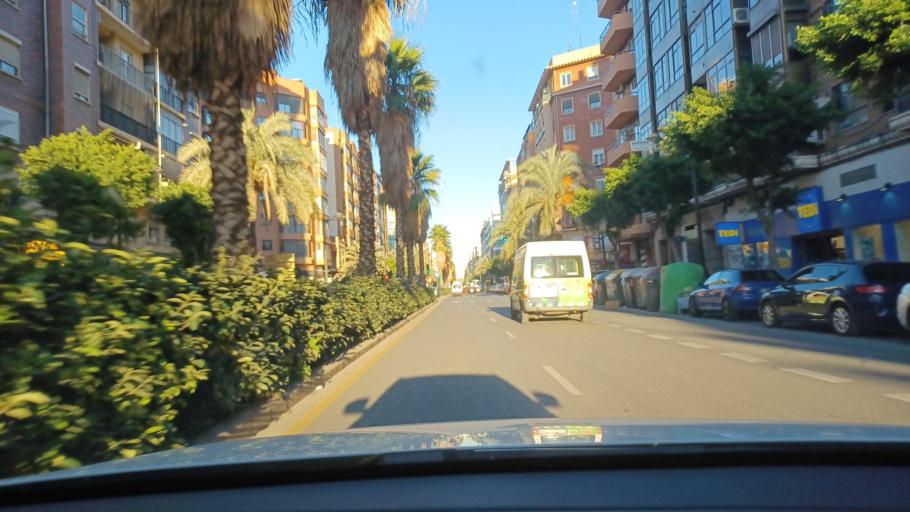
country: ES
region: Valencia
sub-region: Provincia de Valencia
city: Valencia
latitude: 39.4578
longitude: -0.3735
